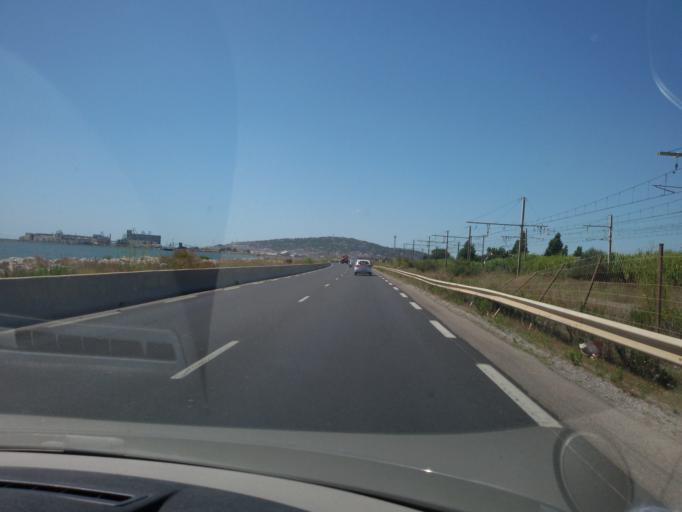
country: FR
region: Languedoc-Roussillon
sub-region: Departement de l'Herault
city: Frontignan
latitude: 43.4221
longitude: 3.7400
